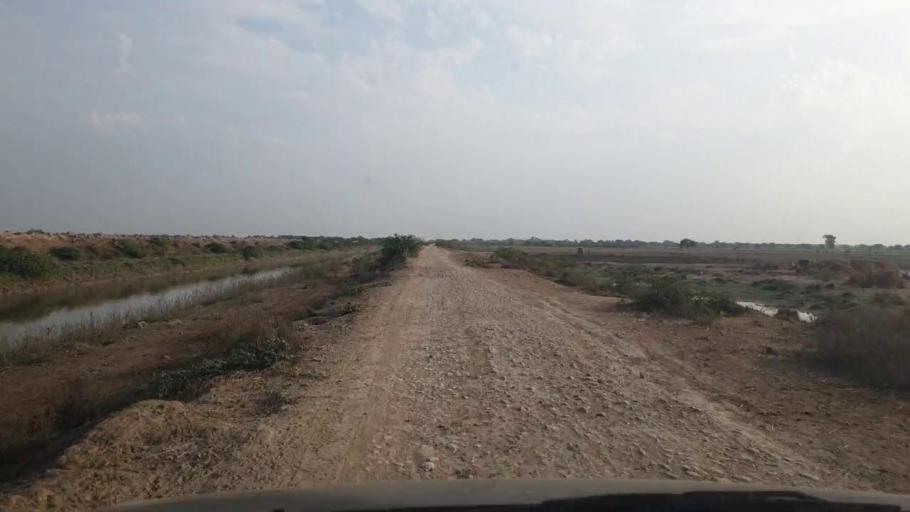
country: PK
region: Sindh
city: Badin
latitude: 24.5581
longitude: 68.6691
